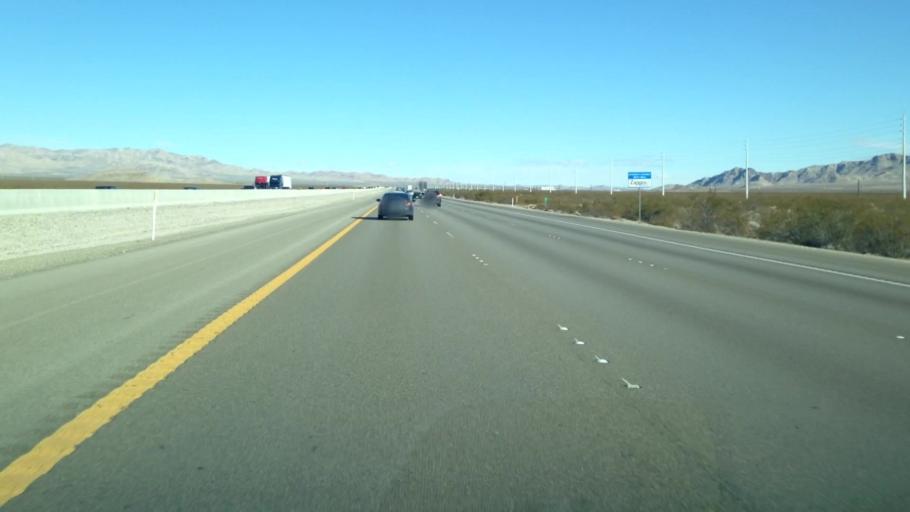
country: US
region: Nevada
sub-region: Clark County
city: Sandy Valley
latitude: 35.7053
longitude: -115.3683
